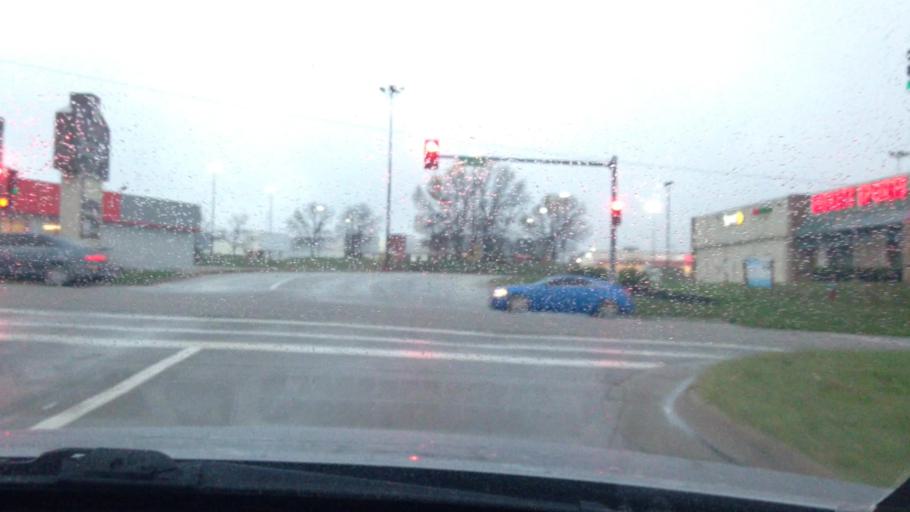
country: US
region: Kansas
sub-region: Leavenworth County
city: Leavenworth
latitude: 39.2850
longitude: -94.9041
